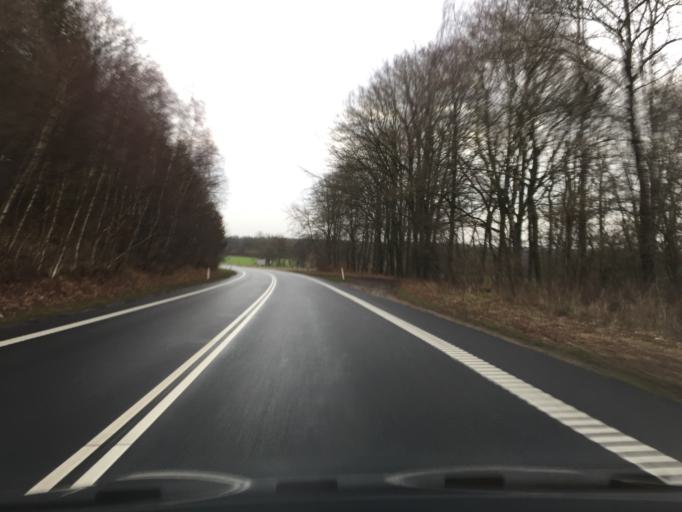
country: DK
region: Central Jutland
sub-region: Viborg Kommune
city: Bjerringbro
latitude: 56.3606
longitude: 9.5916
